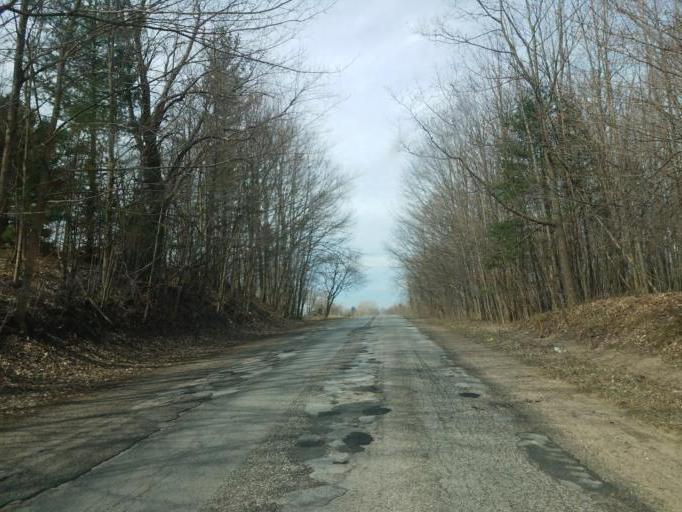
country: US
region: Michigan
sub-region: Oceana County
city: Shelby
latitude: 43.5588
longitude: -86.4184
